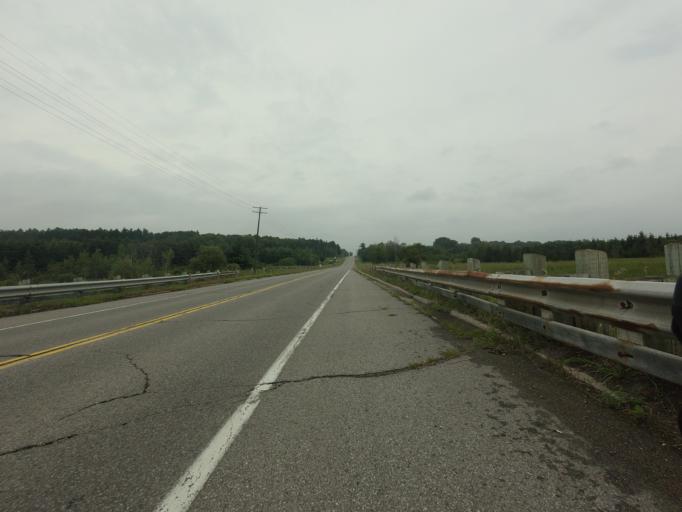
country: CA
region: Ontario
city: Bells Corners
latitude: 45.3403
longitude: -76.0144
